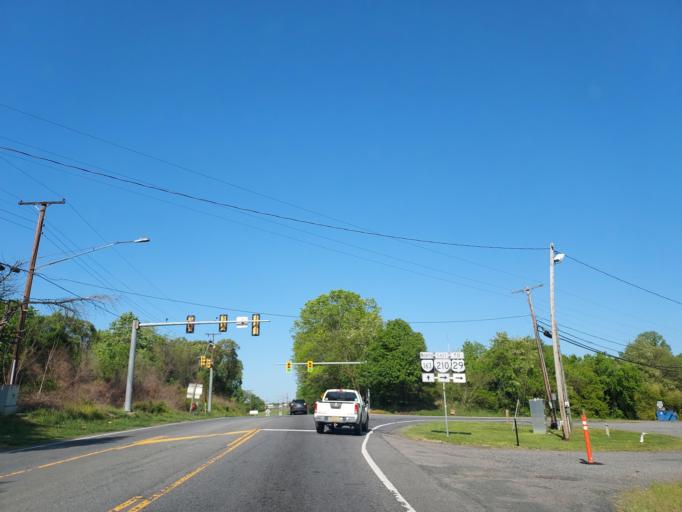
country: US
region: Virginia
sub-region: Amherst County
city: Madison Heights
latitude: 37.4258
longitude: -79.1312
